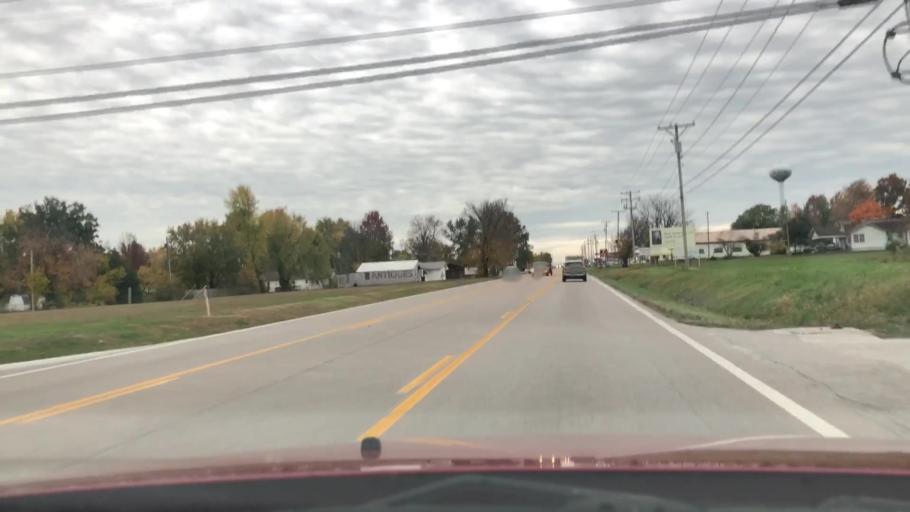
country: US
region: Missouri
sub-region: Dallas County
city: Buffalo
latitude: 37.6478
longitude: -93.1041
